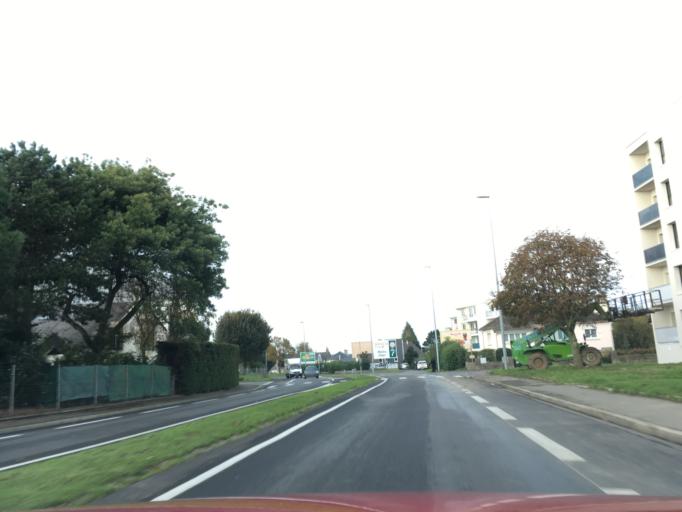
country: FR
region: Lower Normandy
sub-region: Departement de la Manche
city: Donville-les-Bains
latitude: 48.8355
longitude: -1.5705
